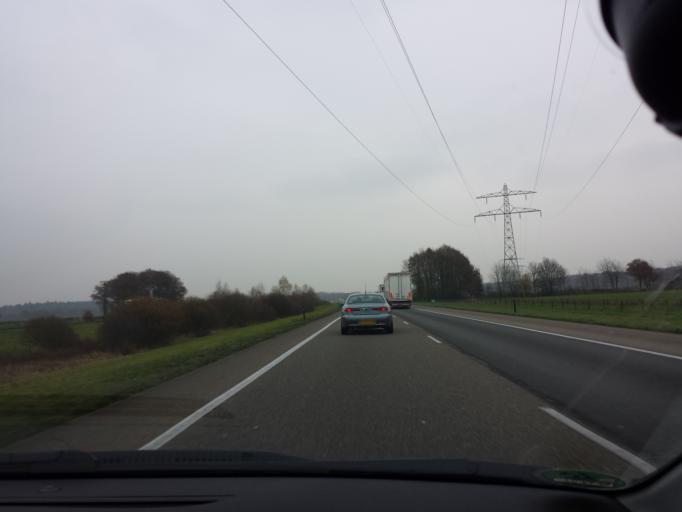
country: NL
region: Gelderland
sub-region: Gemeente Nijmegen
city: Lindenholt
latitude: 51.7879
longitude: 5.8171
